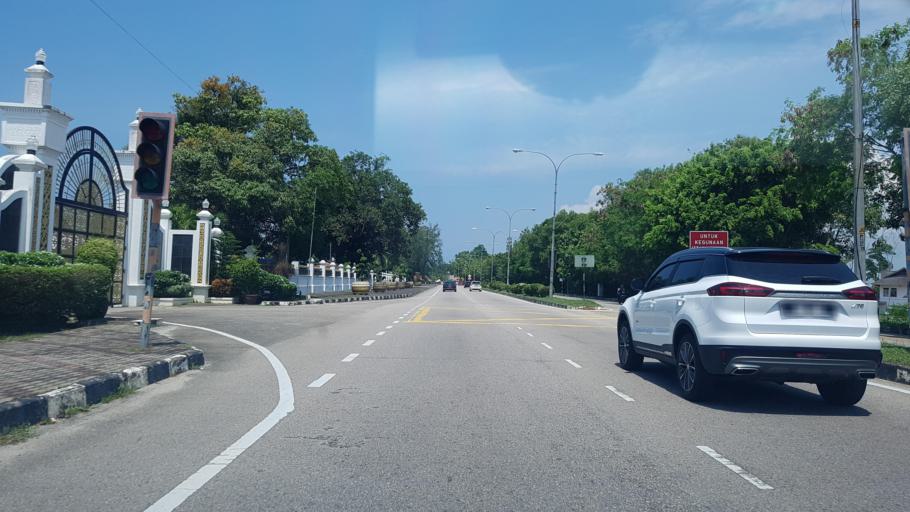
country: MY
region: Terengganu
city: Kuala Terengganu
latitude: 5.3047
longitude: 103.1602
